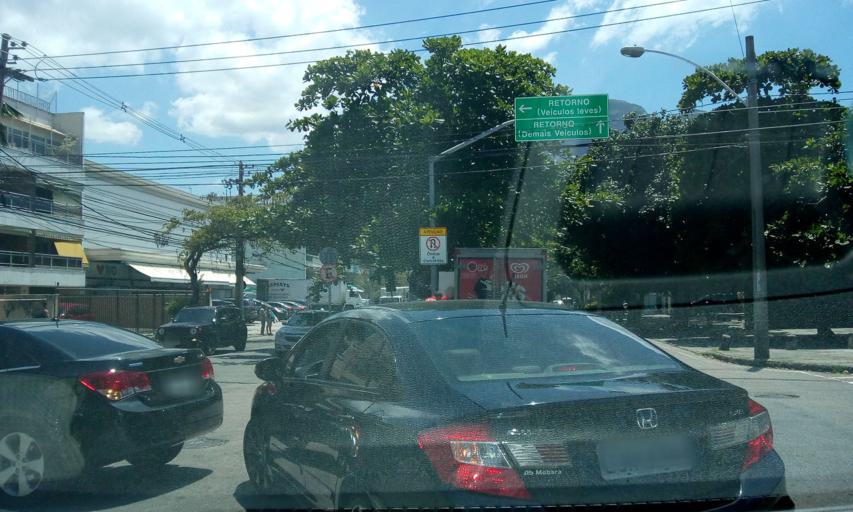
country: BR
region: Rio de Janeiro
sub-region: Rio De Janeiro
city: Rio de Janeiro
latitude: -23.0128
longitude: -43.3118
